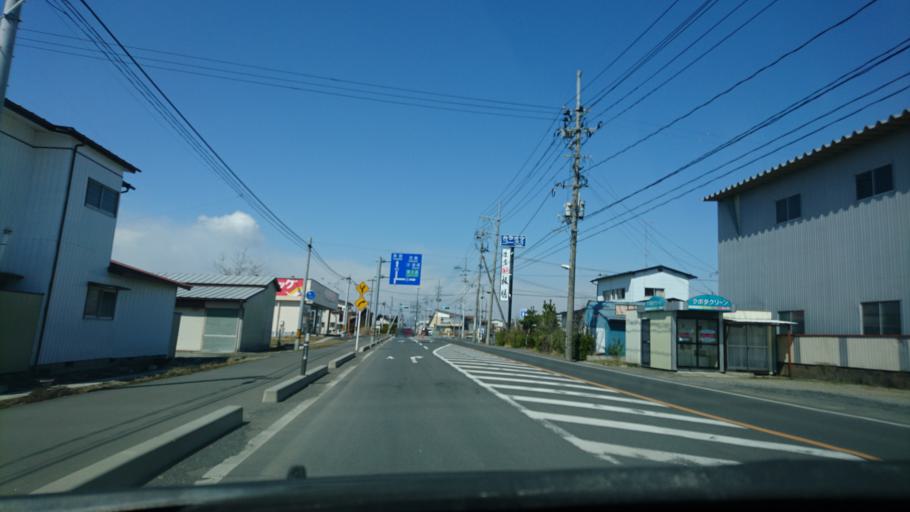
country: JP
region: Iwate
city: Ichinoseki
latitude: 38.7711
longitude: 141.1462
